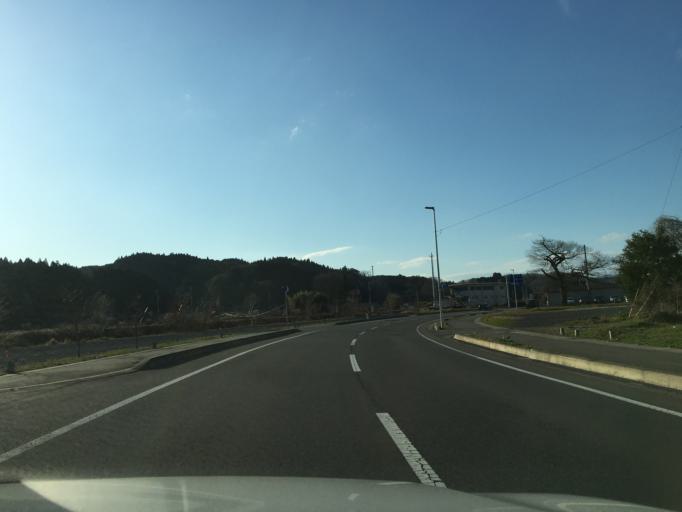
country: JP
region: Ibaraki
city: Daigo
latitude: 36.7688
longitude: 140.3532
